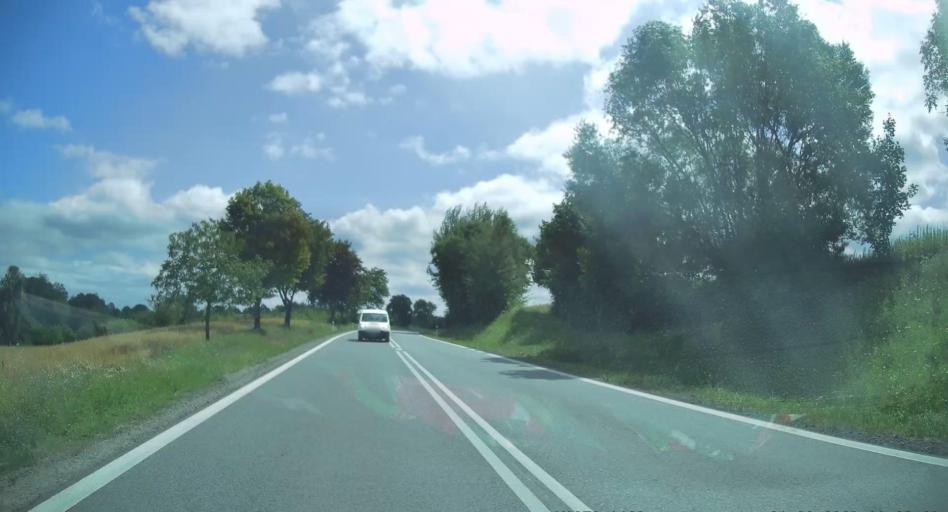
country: PL
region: Swietokrzyskie
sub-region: Powiat sandomierski
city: Klimontow
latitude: 50.6313
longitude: 21.4724
